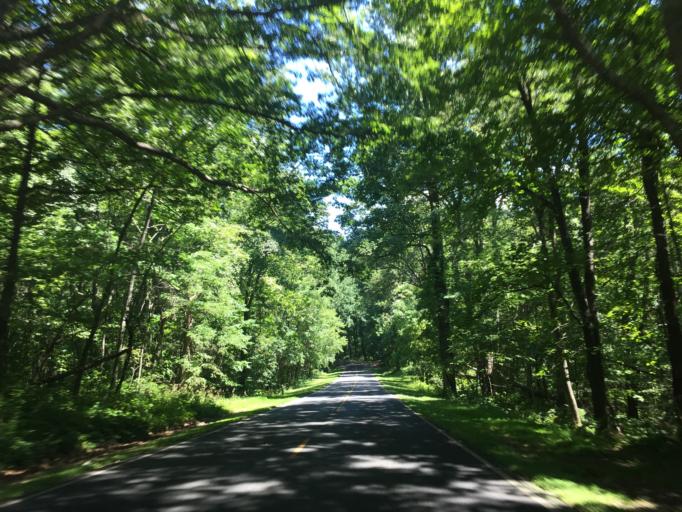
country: US
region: Virginia
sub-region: Warren County
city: Front Royal
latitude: 38.8366
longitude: -78.1956
